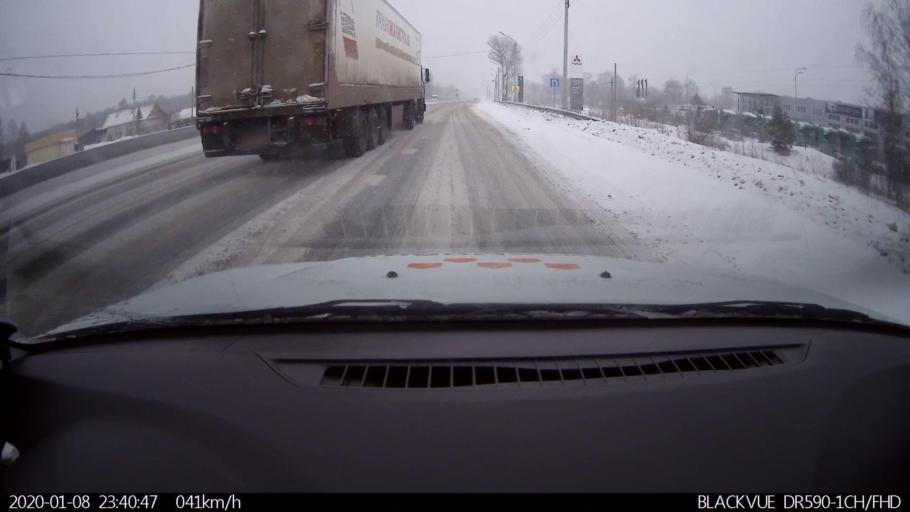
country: RU
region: Nizjnij Novgorod
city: Gorbatovka
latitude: 56.3067
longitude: 43.6927
